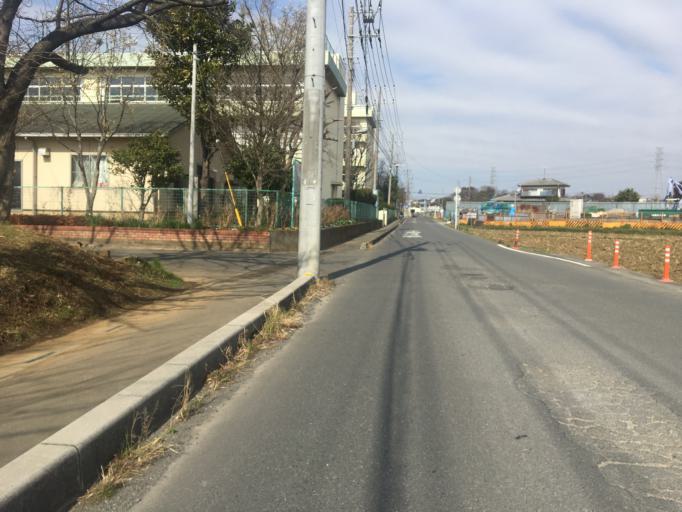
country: JP
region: Saitama
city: Shiki
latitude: 35.8387
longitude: 139.5714
